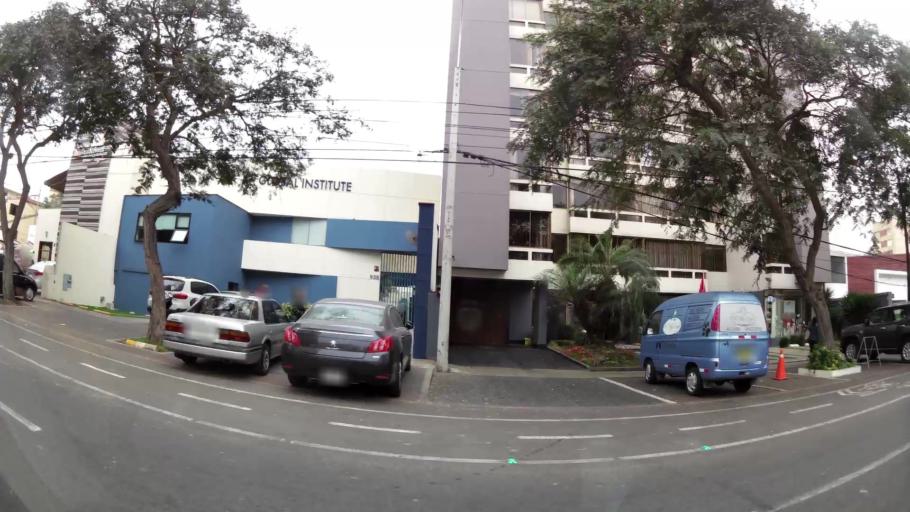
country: PE
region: Lima
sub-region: Lima
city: San Isidro
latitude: -12.0917
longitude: -77.0409
